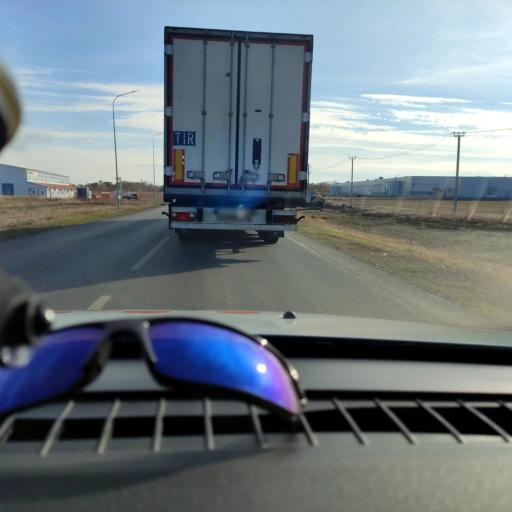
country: RU
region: Samara
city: Samara
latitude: 53.0901
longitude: 50.1354
